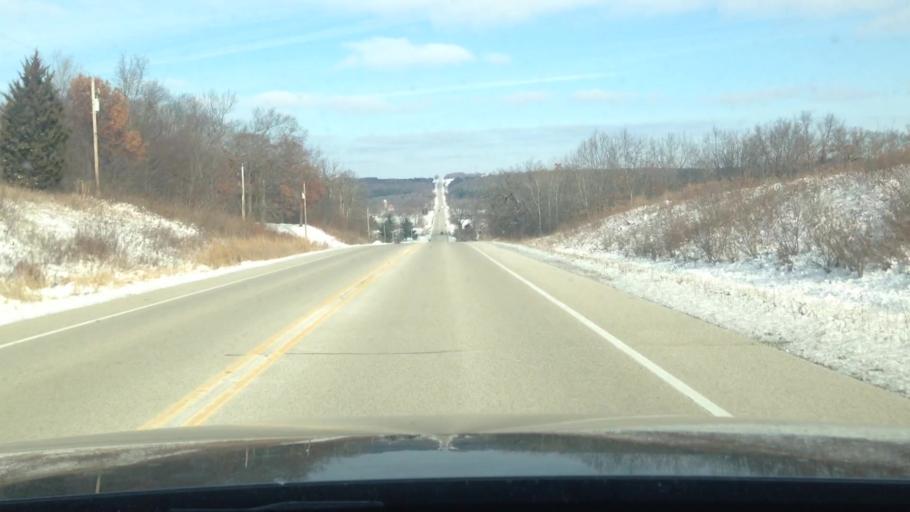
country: US
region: Wisconsin
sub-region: Walworth County
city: East Troy
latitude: 42.7172
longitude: -88.4054
